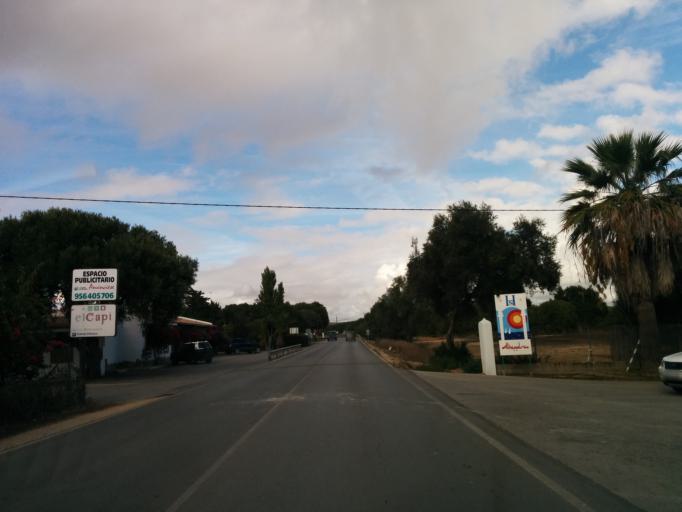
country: ES
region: Andalusia
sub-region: Provincia de Cadiz
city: Vejer de la Frontera
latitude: 36.2033
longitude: -6.0350
